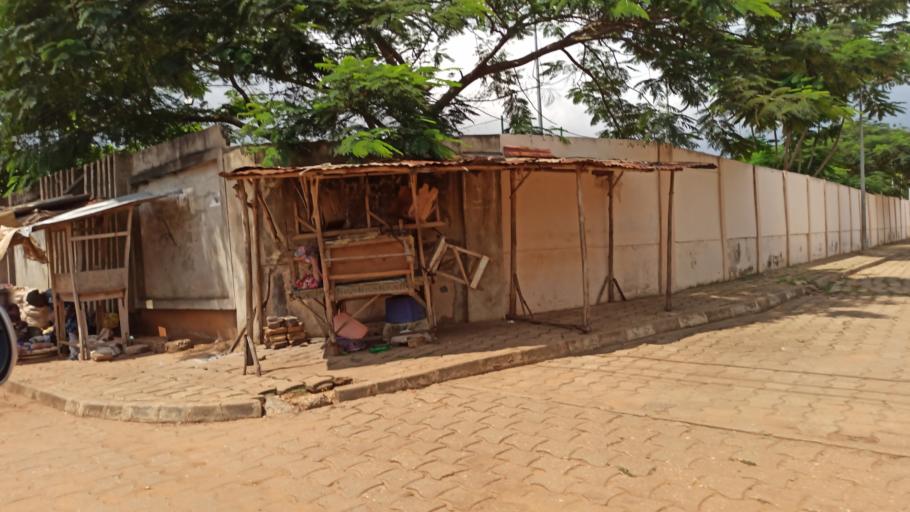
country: BJ
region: Queme
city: Porto-Novo
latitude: 6.4750
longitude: 2.6174
